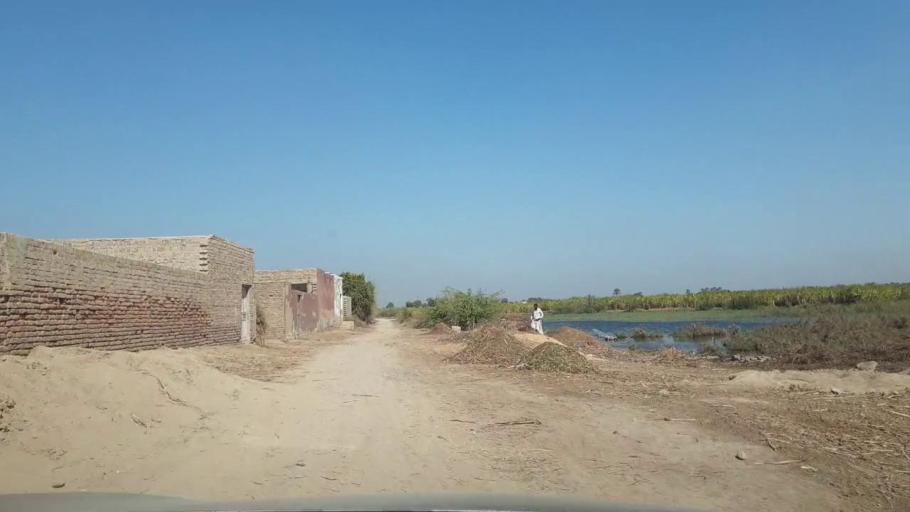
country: PK
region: Sindh
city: Tando Adam
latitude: 25.6317
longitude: 68.6670
